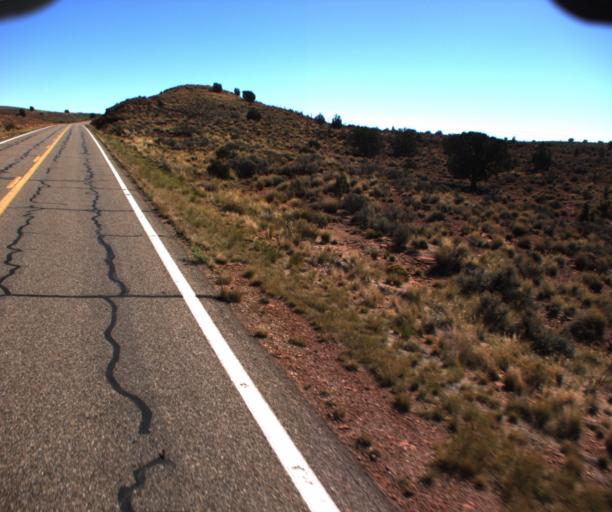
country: US
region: Arizona
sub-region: Coconino County
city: Fredonia
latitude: 36.9073
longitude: -112.4008
